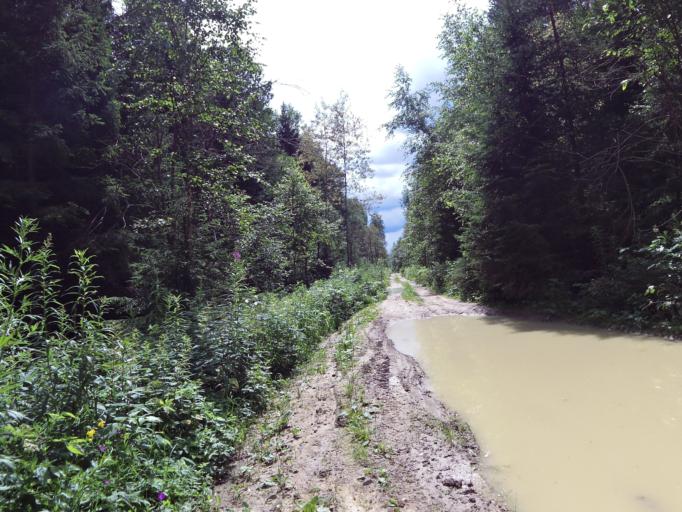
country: RU
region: Moskovskaya
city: Popovo
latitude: 54.9776
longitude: 37.6948
